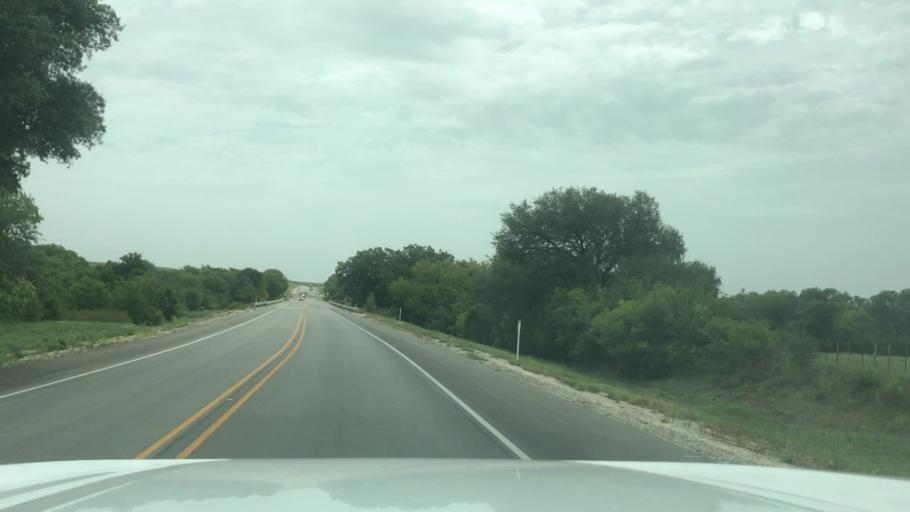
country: US
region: Texas
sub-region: Erath County
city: Dublin
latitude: 32.0745
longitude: -98.2318
